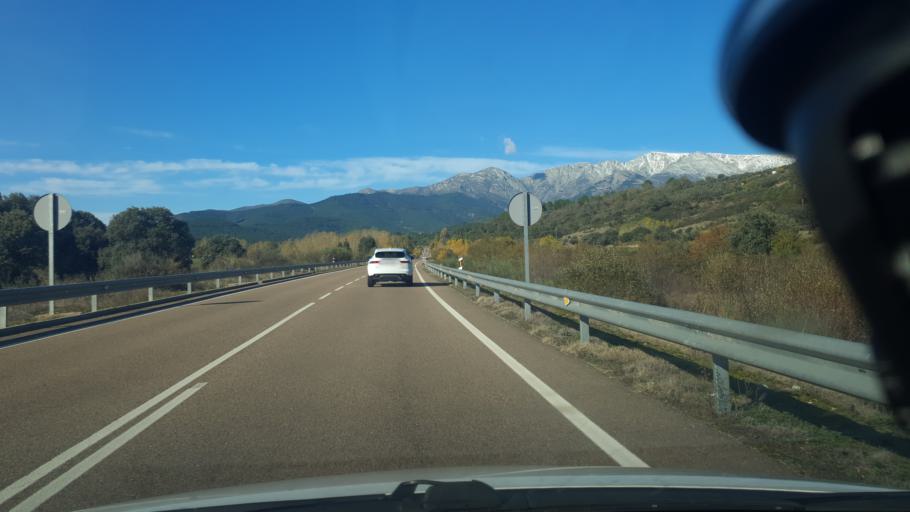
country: ES
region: Castille and Leon
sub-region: Provincia de Avila
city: Arenas de San Pedro
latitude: 40.1865
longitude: -5.0583
